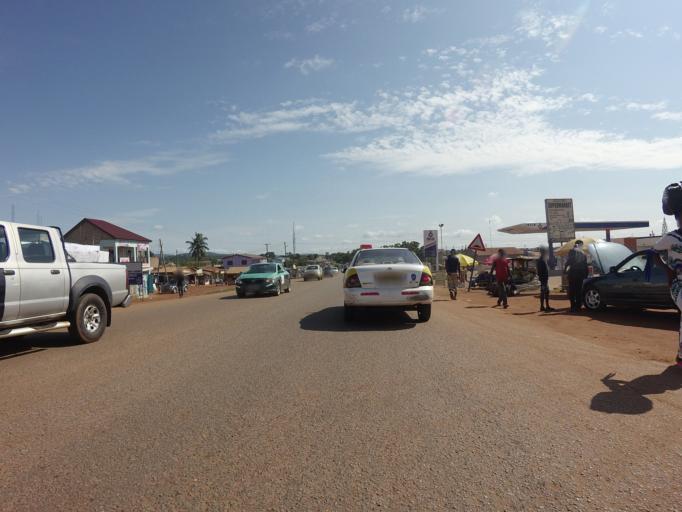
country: GH
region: Greater Accra
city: Medina Estates
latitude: 5.7439
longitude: -0.1527
